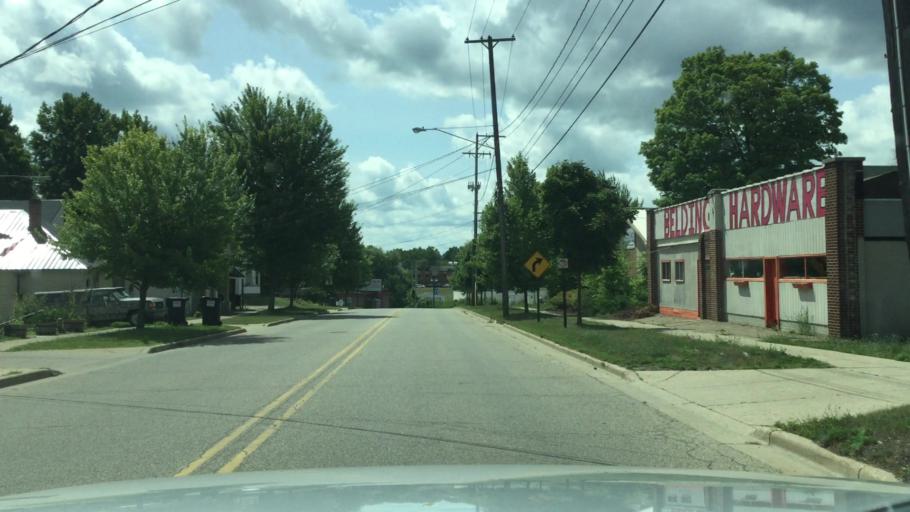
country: US
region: Michigan
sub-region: Ionia County
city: Belding
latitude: 43.1019
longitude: -85.2279
